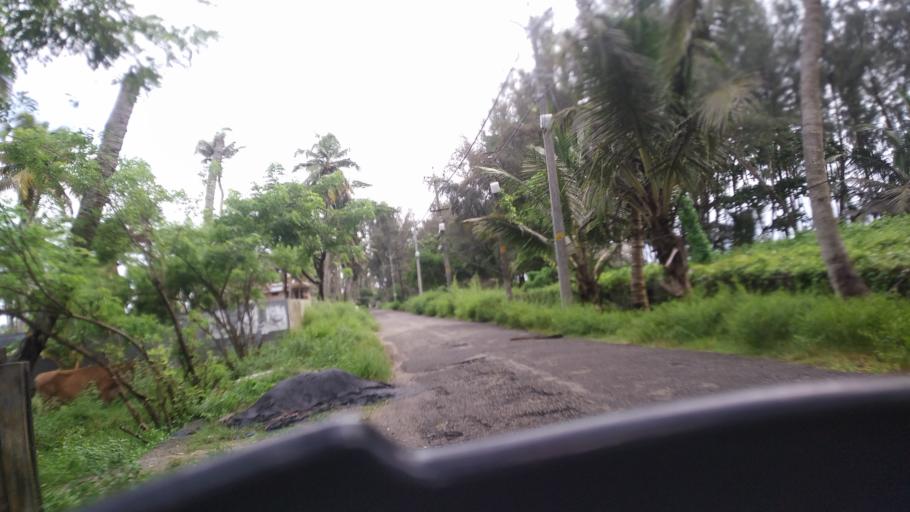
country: IN
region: Kerala
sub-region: Ernakulam
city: Elur
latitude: 10.1132
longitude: 76.1869
